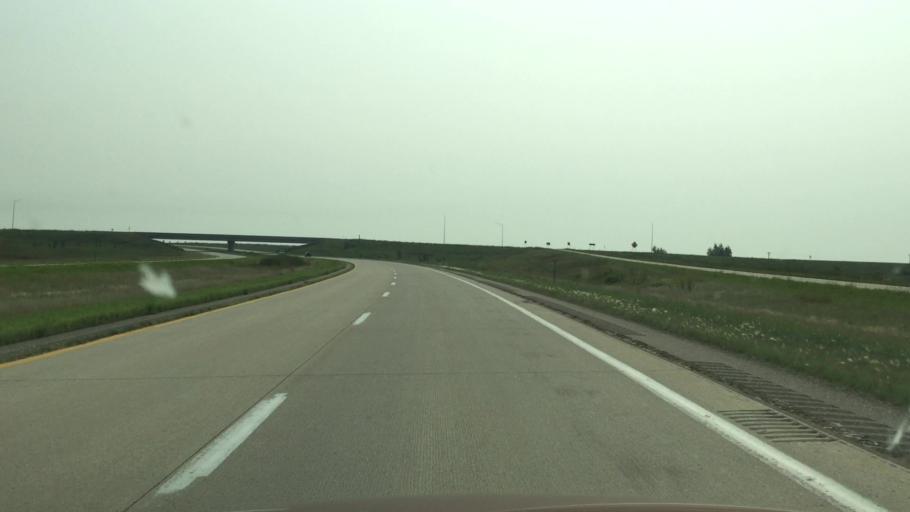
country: US
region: Iowa
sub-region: O'Brien County
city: Sheldon
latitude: 43.1640
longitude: -95.8275
